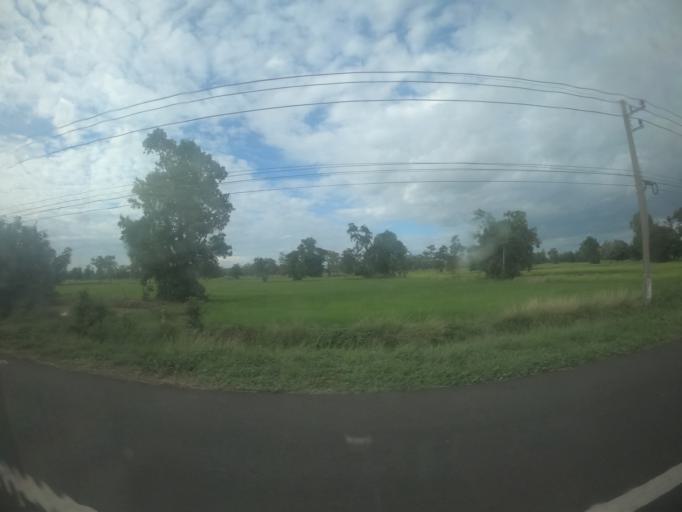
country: TH
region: Surin
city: Prasat
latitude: 14.5971
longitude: 103.4400
